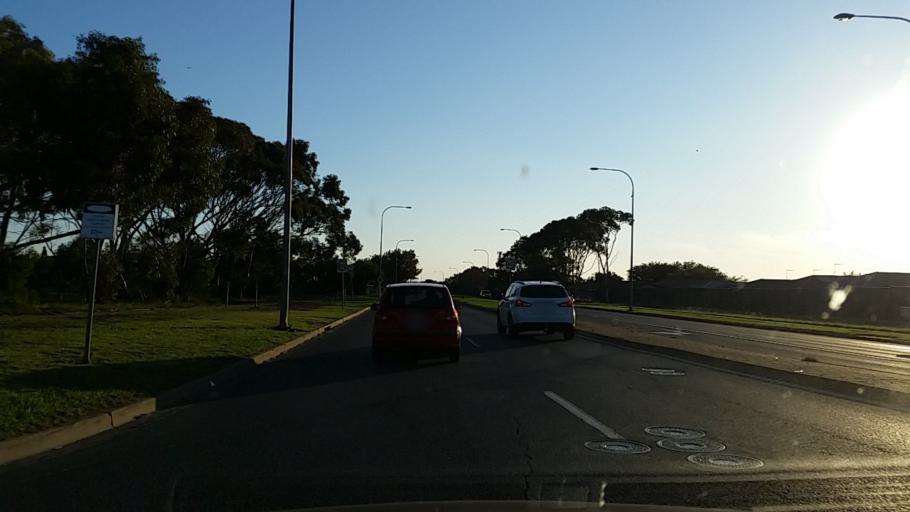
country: AU
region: South Australia
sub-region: Onkaparinga
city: Seaford
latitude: -35.1908
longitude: 138.4900
